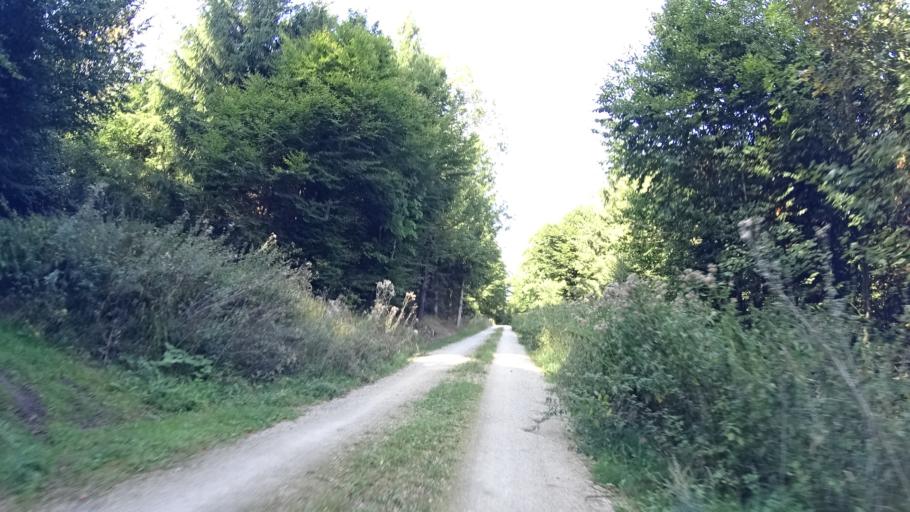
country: DE
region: Bavaria
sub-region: Regierungsbezirk Mittelfranken
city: Greding
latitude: 48.9729
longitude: 11.3502
